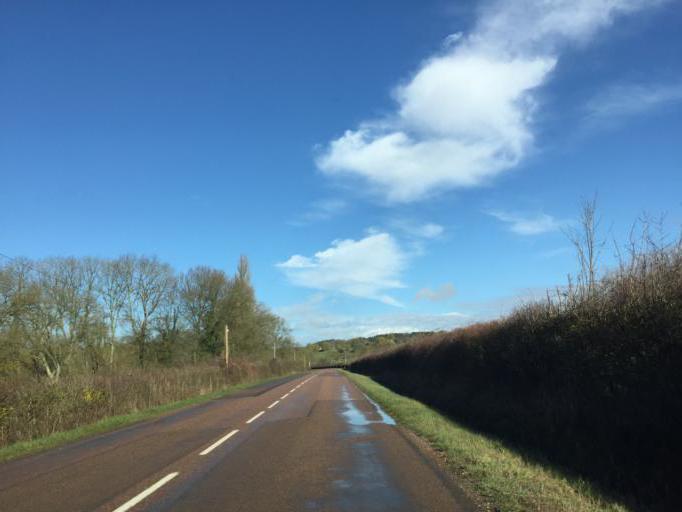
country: FR
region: Bourgogne
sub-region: Departement de la Nievre
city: Clamecy
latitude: 47.4643
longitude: 3.4528
